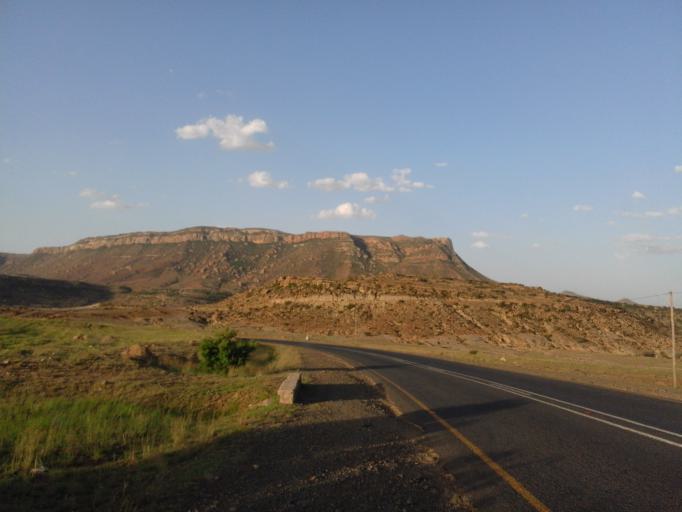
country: LS
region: Mafeteng
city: Mafeteng
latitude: -29.8961
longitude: 27.2552
